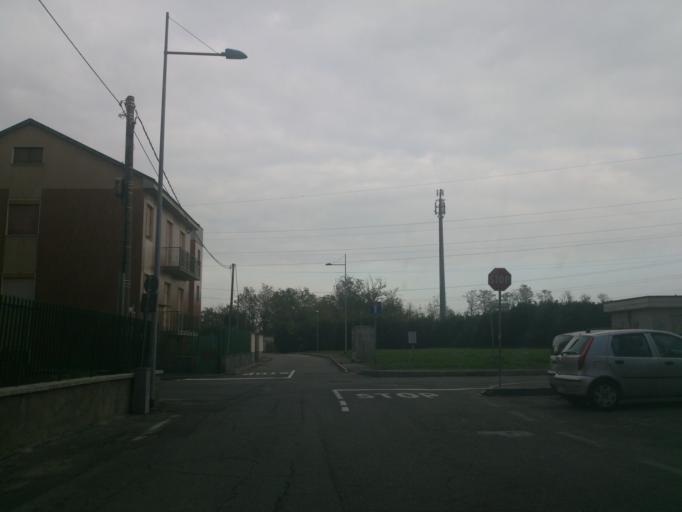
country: IT
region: Lombardy
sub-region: Citta metropolitana di Milano
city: Poasco-Sorigherio
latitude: 45.4058
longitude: 9.2328
